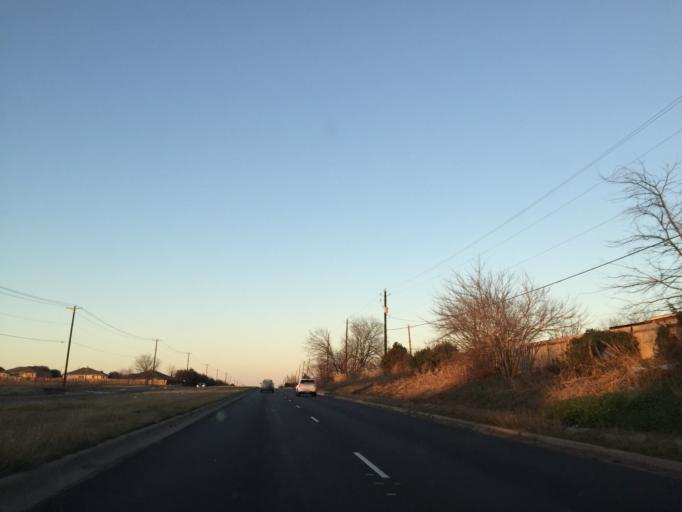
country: US
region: Texas
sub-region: Travis County
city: Pflugerville
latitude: 30.4144
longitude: -97.6327
